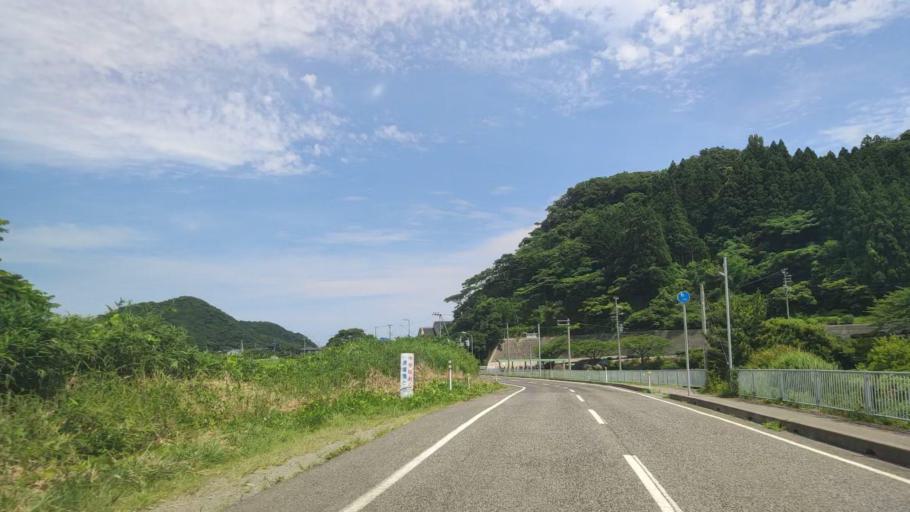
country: JP
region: Hyogo
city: Toyooka
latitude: 35.6510
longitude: 134.7636
